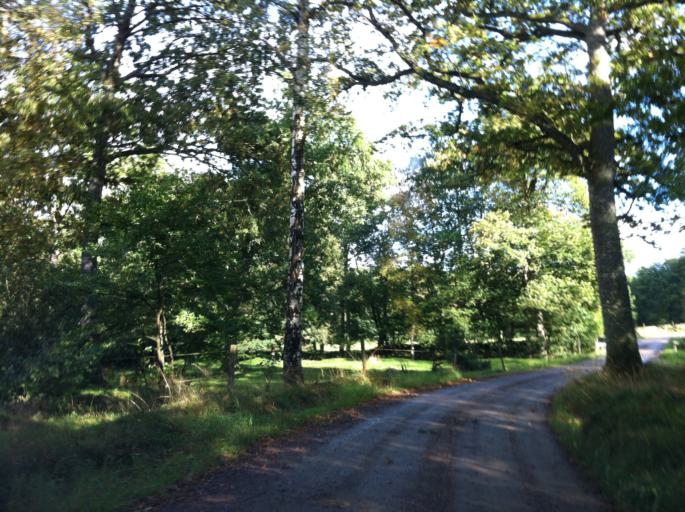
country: SE
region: Skane
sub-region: Hassleholms Kommun
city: Sosdala
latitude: 56.1256
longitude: 13.5940
